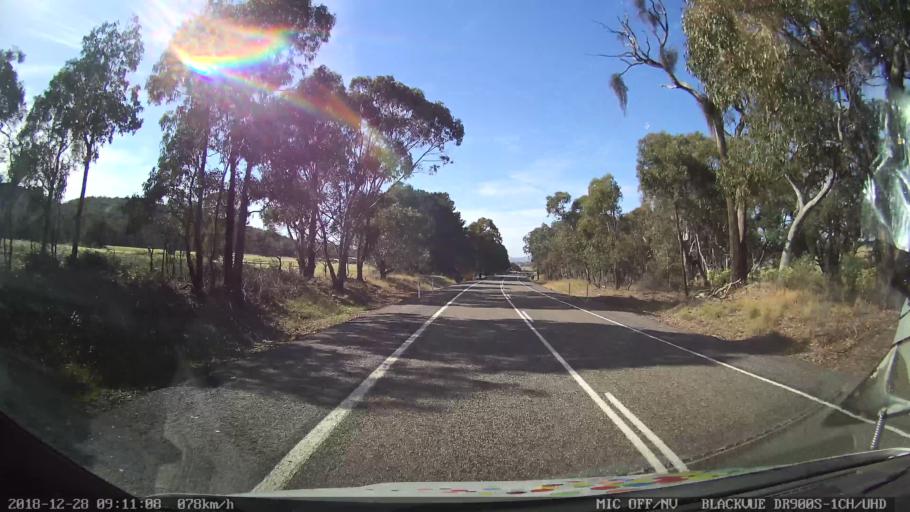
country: AU
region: New South Wales
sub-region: Upper Lachlan Shire
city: Crookwell
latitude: -34.2401
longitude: 149.3383
